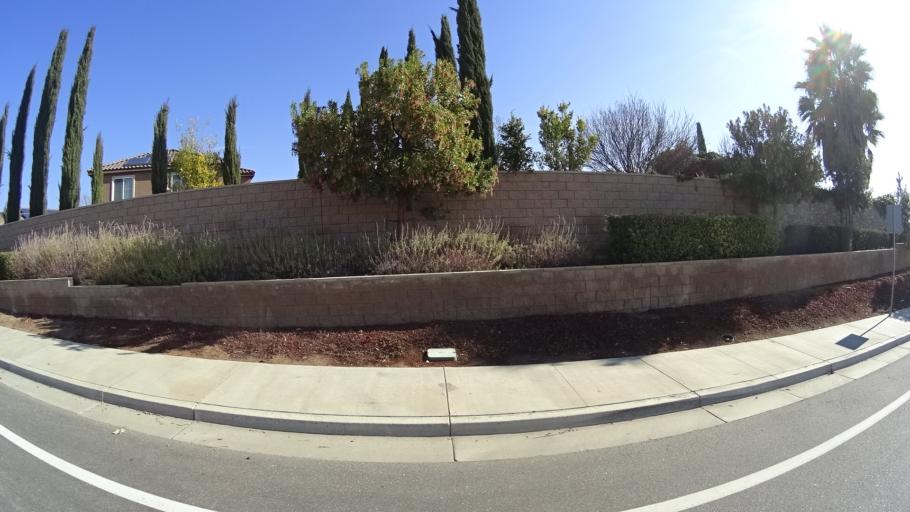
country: US
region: California
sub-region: Kern County
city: Oildale
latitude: 35.4021
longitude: -118.8962
